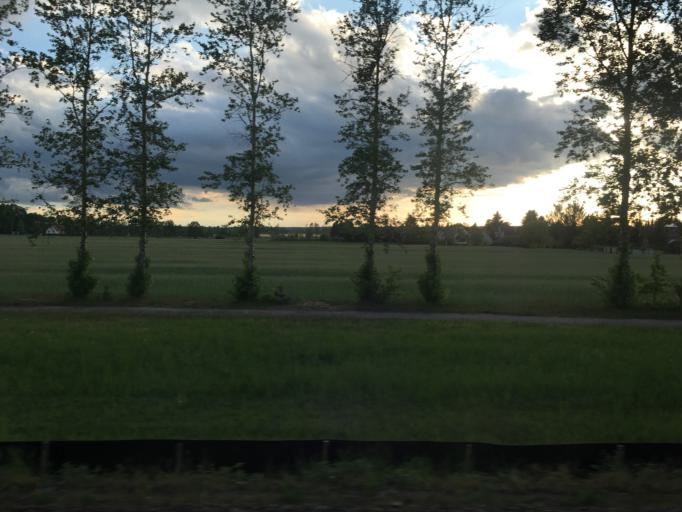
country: DE
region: Brandenburg
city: Ruckersdorf
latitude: 51.5738
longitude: 13.5738
